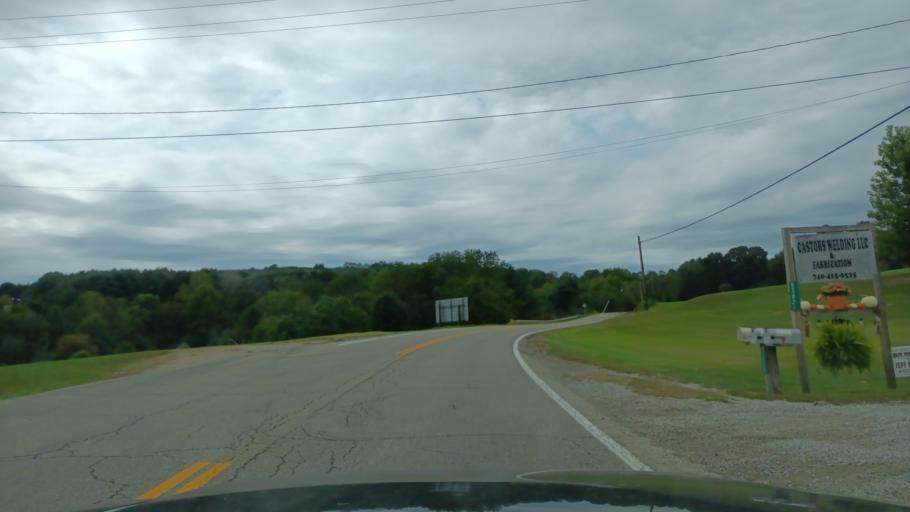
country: US
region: Ohio
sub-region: Vinton County
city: McArthur
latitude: 39.2639
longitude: -82.5112
